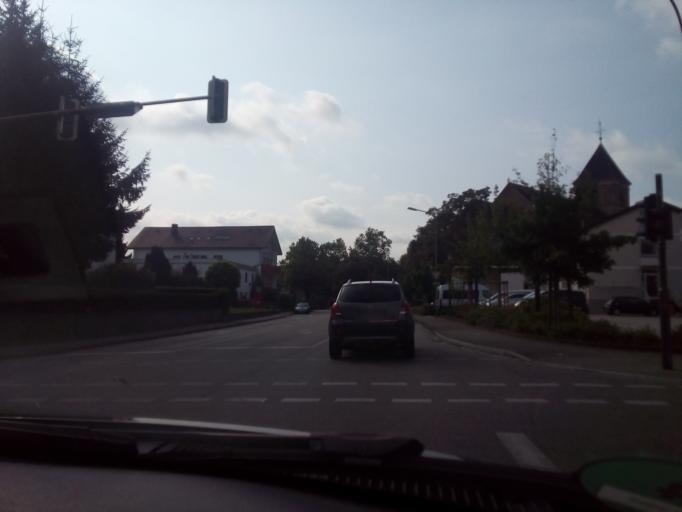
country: DE
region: Baden-Wuerttemberg
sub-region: Freiburg Region
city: Achern
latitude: 48.6329
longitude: 8.0739
